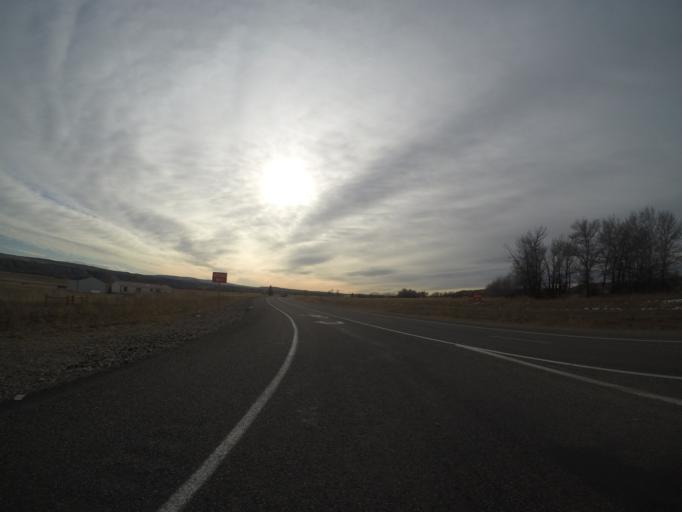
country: US
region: Montana
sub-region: Yellowstone County
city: Laurel
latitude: 45.5374
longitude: -108.8511
